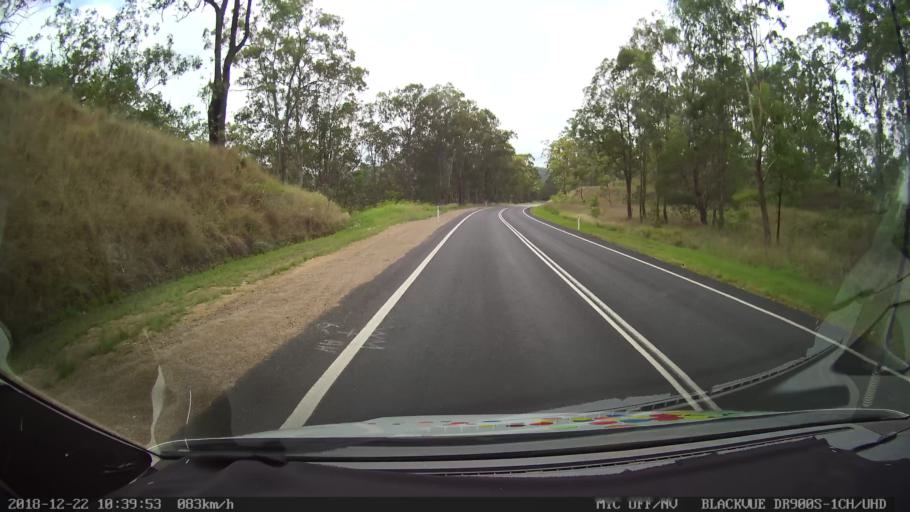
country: AU
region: New South Wales
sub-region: Clarence Valley
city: South Grafton
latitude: -29.6303
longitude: 152.7398
